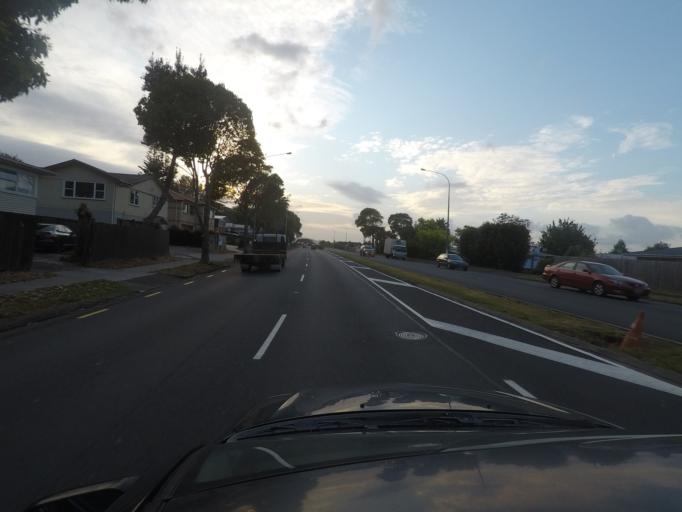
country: NZ
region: Auckland
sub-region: Auckland
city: Tamaki
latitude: -36.9216
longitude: 174.8788
